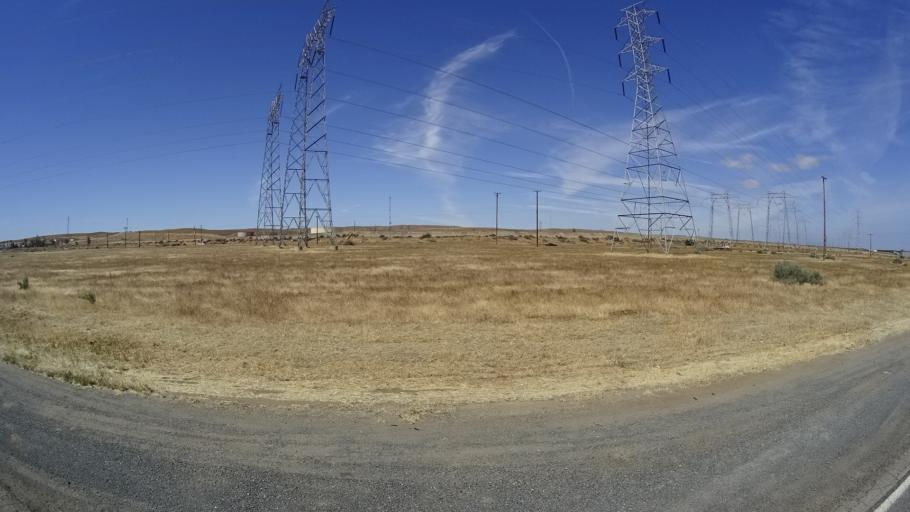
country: US
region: California
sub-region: Kings County
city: Kettleman City
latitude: 35.9981
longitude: -119.9576
